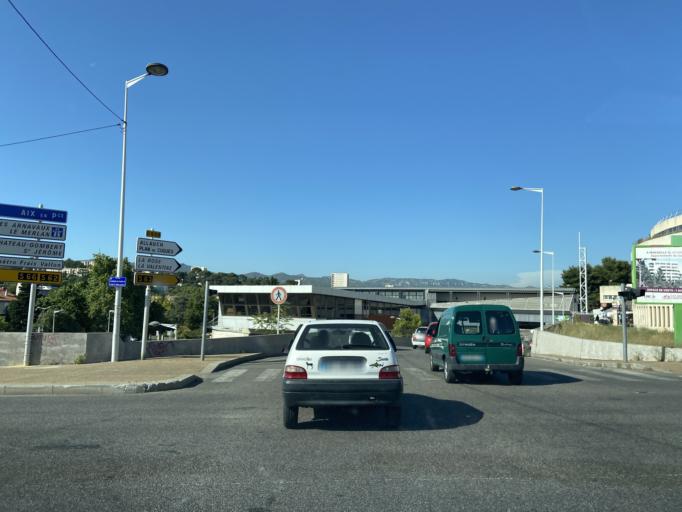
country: FR
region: Provence-Alpes-Cote d'Azur
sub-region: Departement des Bouches-du-Rhone
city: Marseille 13
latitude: 43.3251
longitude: 5.4233
